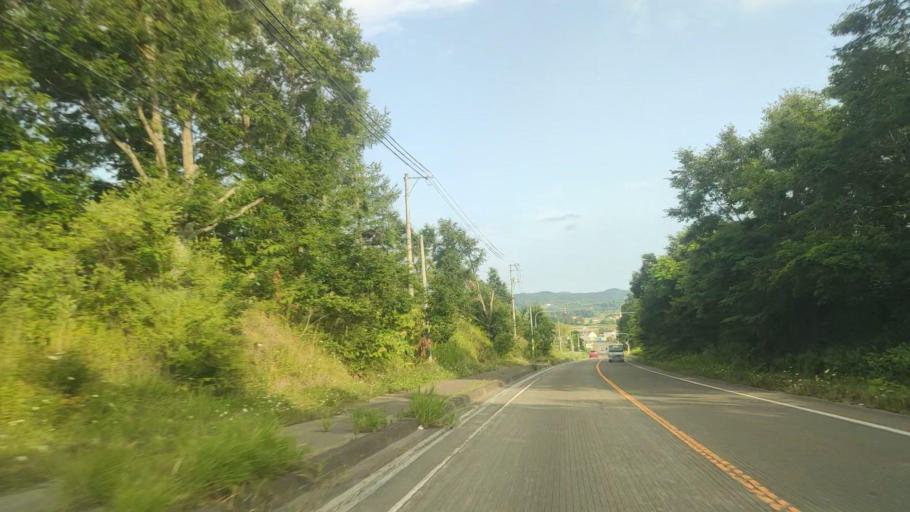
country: JP
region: Hokkaido
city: Iwamizawa
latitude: 43.0231
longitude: 141.8489
